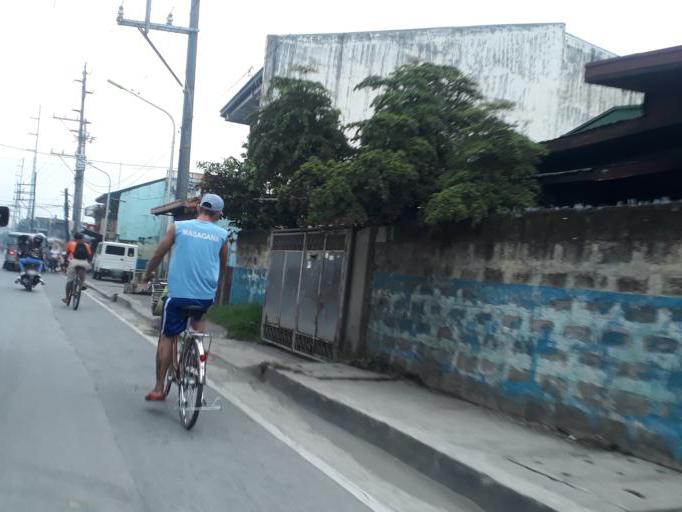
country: PH
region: Metro Manila
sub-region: Caloocan City
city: Niugan
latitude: 14.6824
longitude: 120.9598
